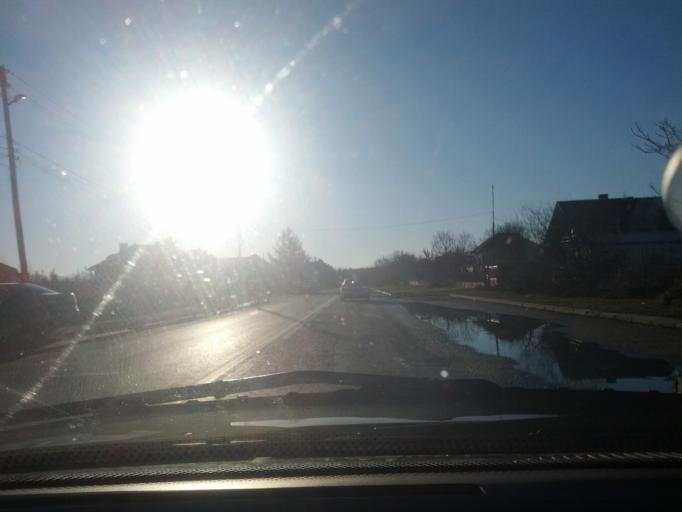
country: BG
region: Vratsa
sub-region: Obshtina Borovan
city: Borovan
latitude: 43.4202
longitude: 23.7451
